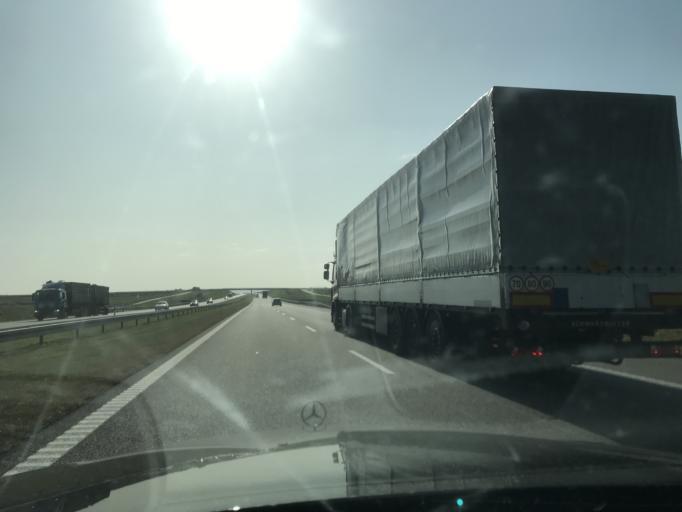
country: PL
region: Subcarpathian Voivodeship
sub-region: Powiat debicki
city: Czarna
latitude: 50.0958
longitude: 21.2914
